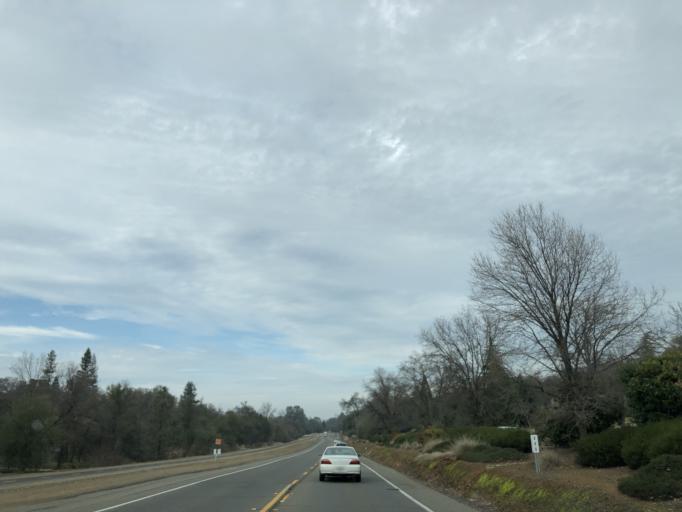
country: US
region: California
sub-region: El Dorado County
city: El Dorado Hills
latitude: 38.6930
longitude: -121.0818
